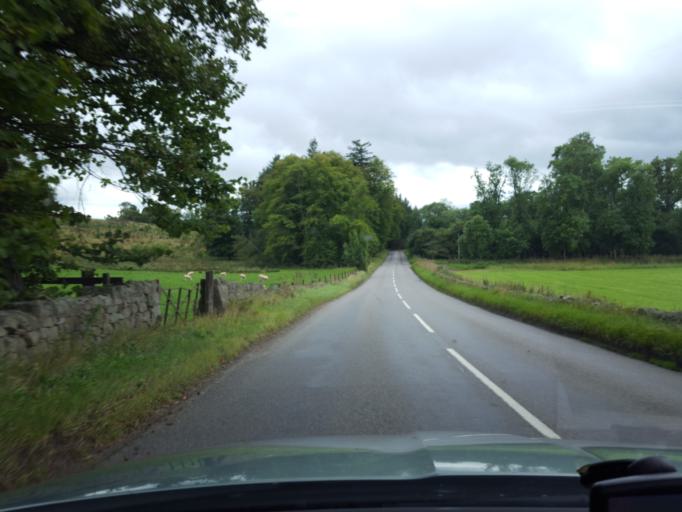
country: GB
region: Scotland
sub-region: Aberdeenshire
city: Kemnay
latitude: 57.1585
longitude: -2.4312
